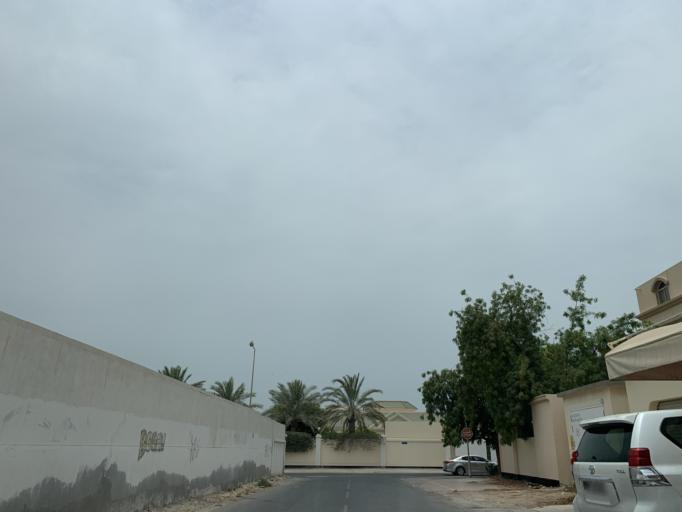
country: BH
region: Northern
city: Madinat `Isa
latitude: 26.1879
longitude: 50.4722
